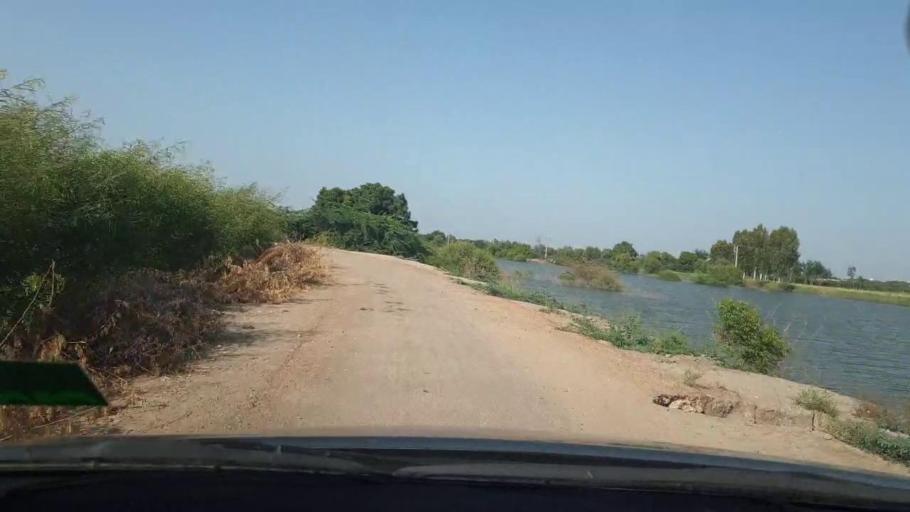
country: PK
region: Sindh
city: Naukot
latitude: 24.8613
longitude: 69.3204
